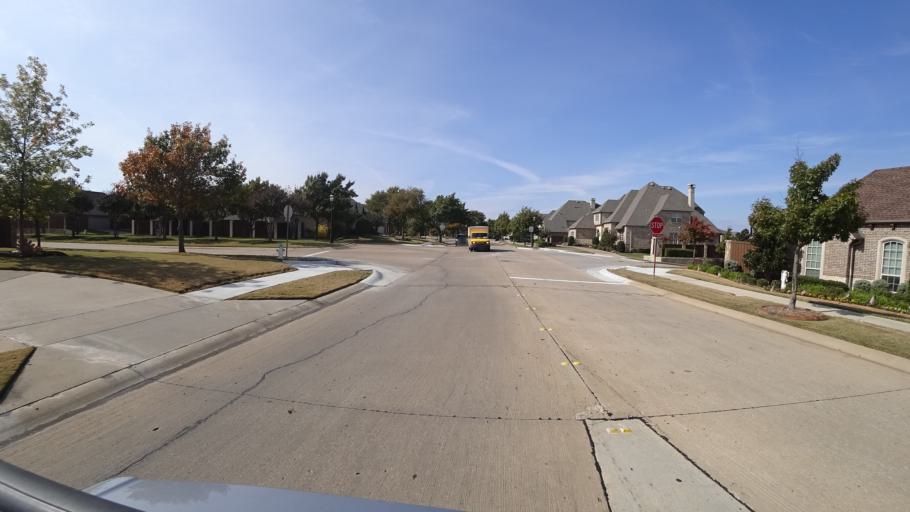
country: US
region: Texas
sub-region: Denton County
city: The Colony
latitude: 33.0366
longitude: -96.8883
